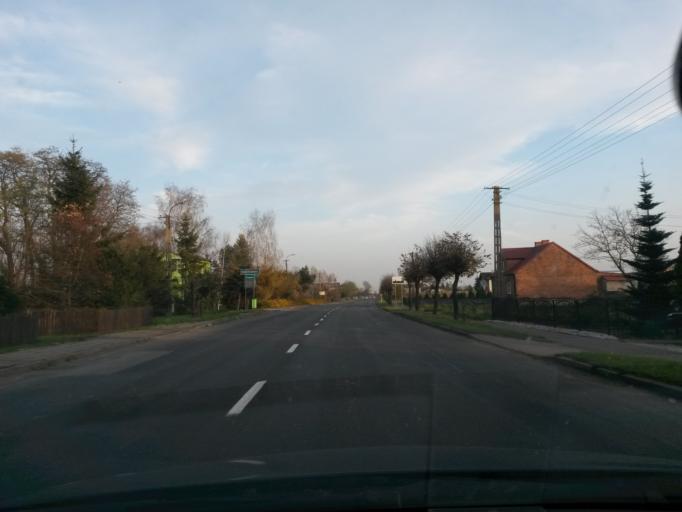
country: PL
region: Lodz Voivodeship
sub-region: Powiat wielunski
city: Mokrsko
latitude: 51.2610
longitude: 18.4773
